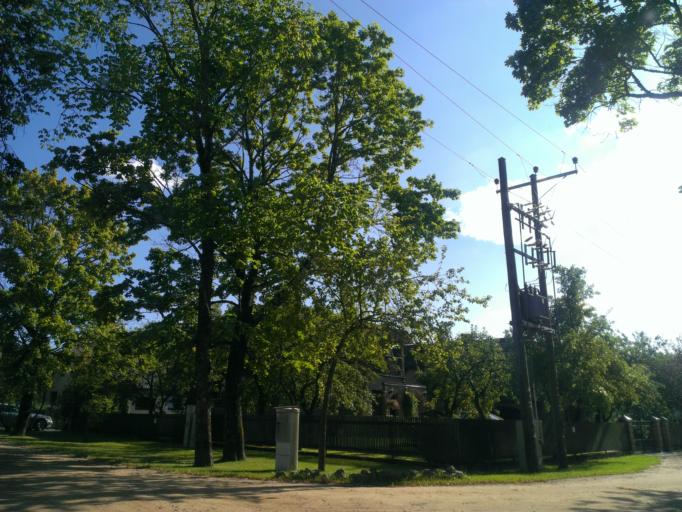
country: LV
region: Sigulda
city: Sigulda
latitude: 57.1649
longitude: 24.8860
